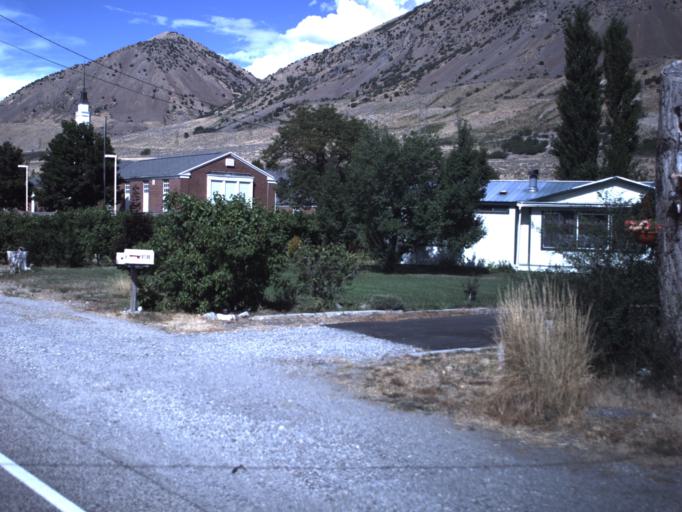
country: US
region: Utah
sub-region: Box Elder County
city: Elwood
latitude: 41.7044
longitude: -112.0901
